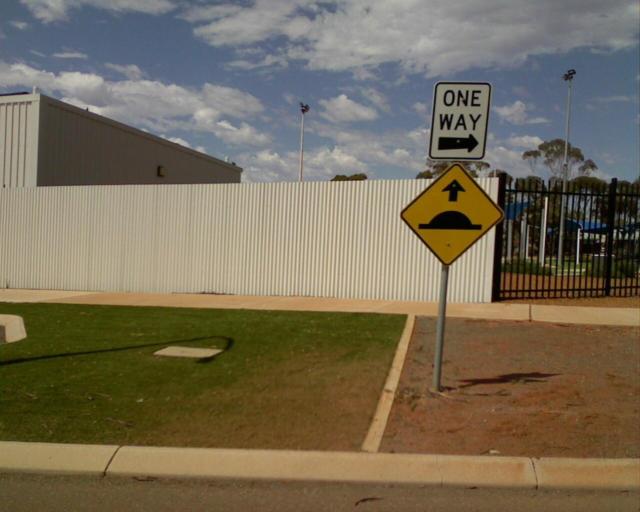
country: AU
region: Western Australia
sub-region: Kalgoorlie/Boulder
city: Stoneville
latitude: -31.2076
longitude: 121.6211
